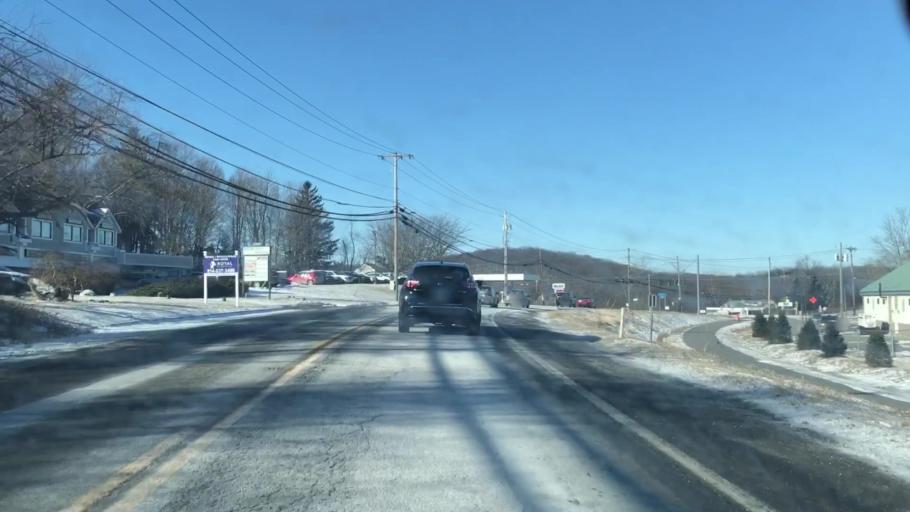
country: US
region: New York
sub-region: Putnam County
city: Brewster
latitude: 41.3990
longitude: -73.6318
